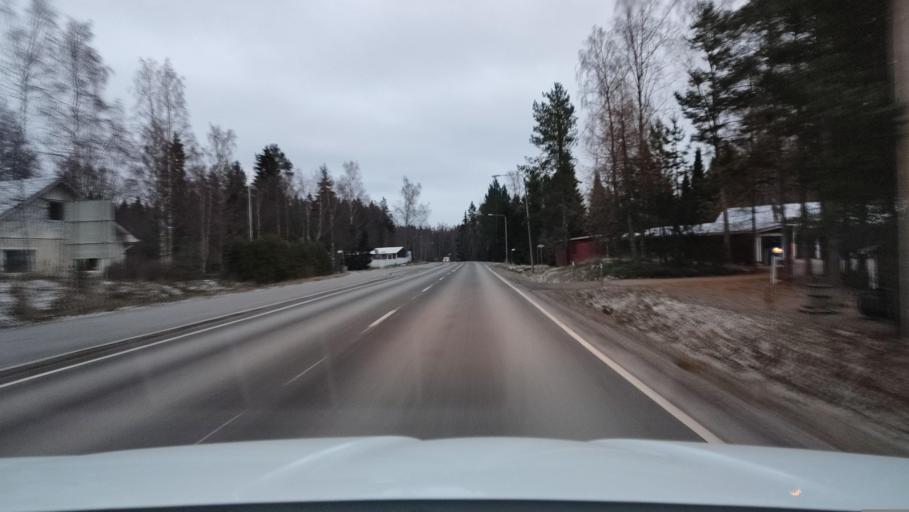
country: FI
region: Ostrobothnia
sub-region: Vaasa
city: Replot
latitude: 63.2196
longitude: 21.4188
